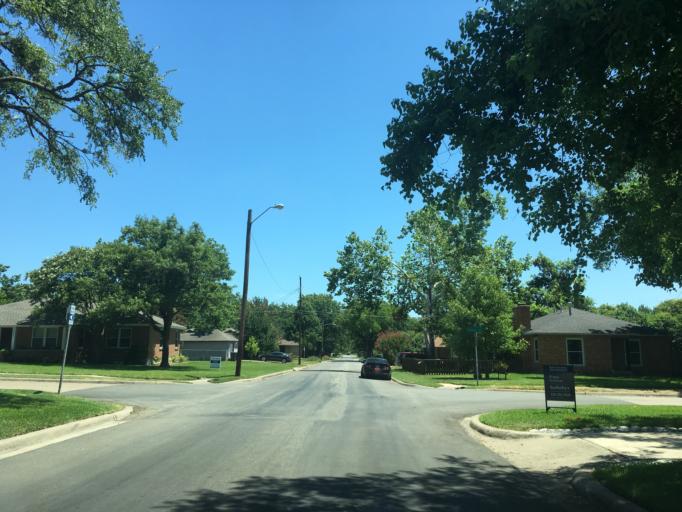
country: US
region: Texas
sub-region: Dallas County
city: Highland Park
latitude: 32.8508
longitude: -96.7126
